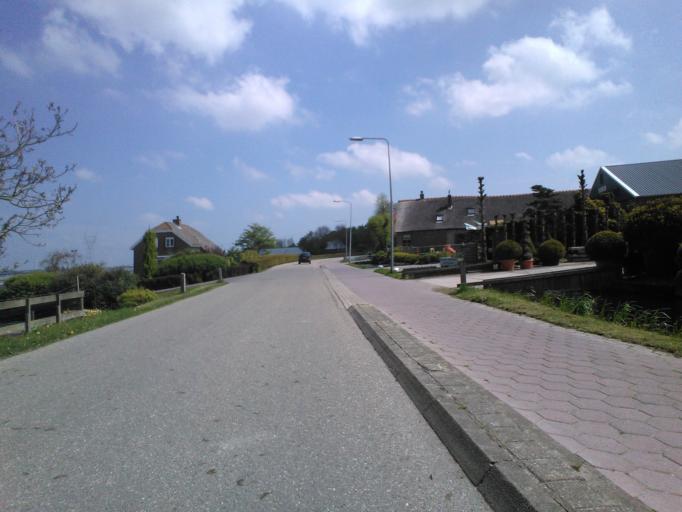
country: NL
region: South Holland
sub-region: Gemeente Rijnwoude
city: Benthuizen
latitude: 52.0968
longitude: 4.5674
